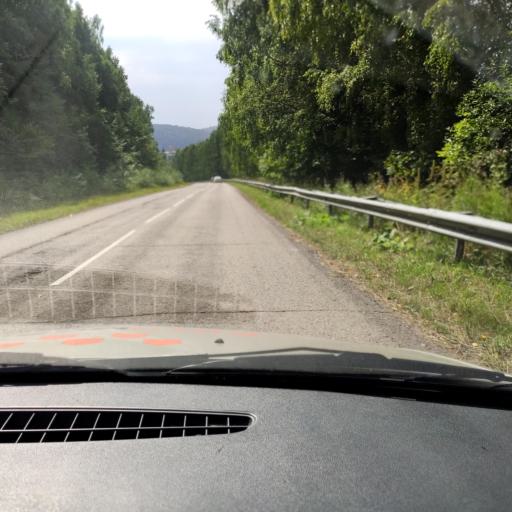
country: RU
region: Bashkortostan
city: Pavlovka
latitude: 55.4123
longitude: 56.5782
